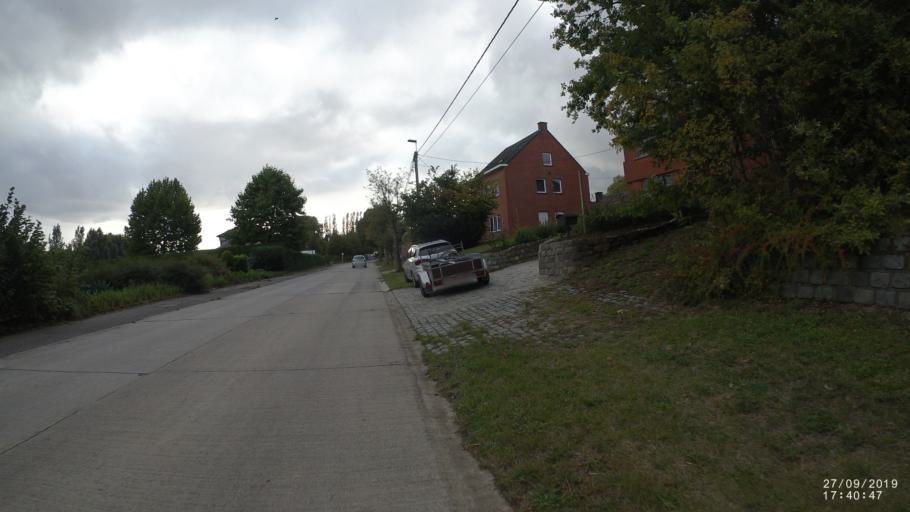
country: BE
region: Flanders
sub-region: Provincie Oost-Vlaanderen
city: Zottegem
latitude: 50.8334
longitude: 3.7571
